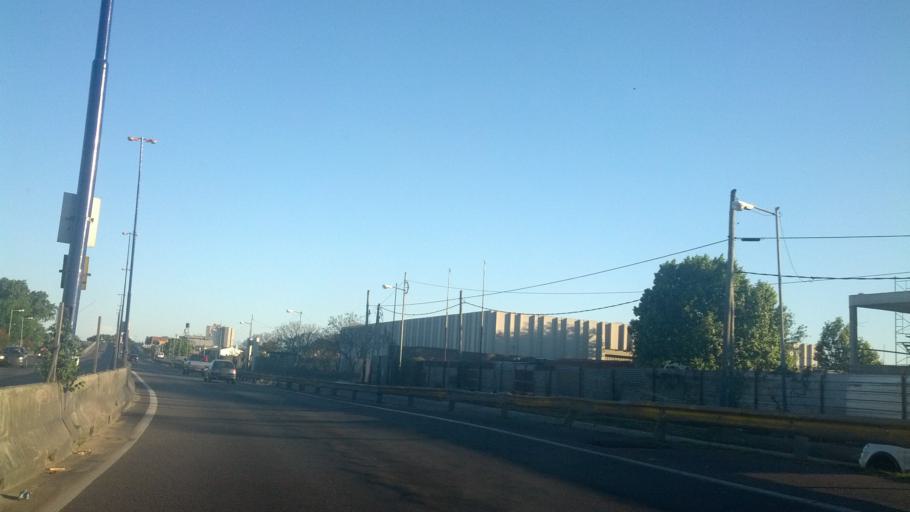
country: AR
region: Buenos Aires
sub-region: Partido de Lomas de Zamora
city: Lomas de Zamora
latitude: -34.7520
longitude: -58.4359
